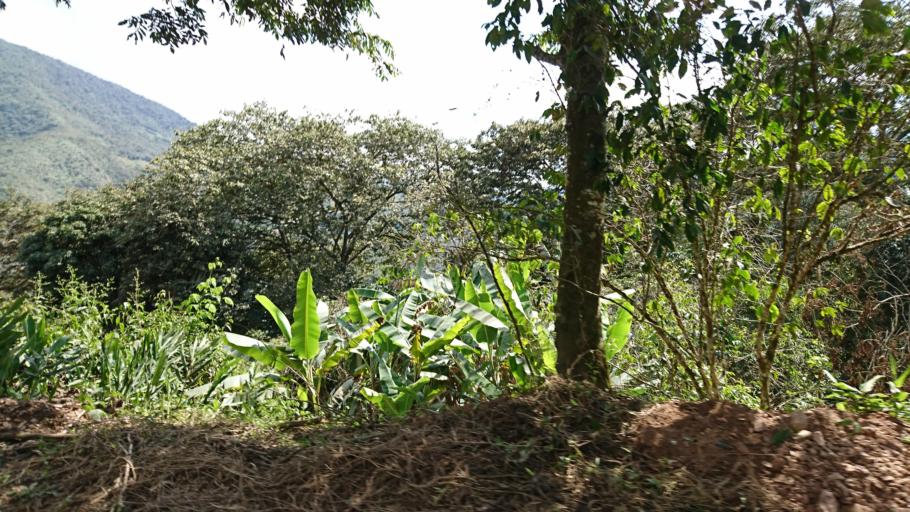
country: BO
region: La Paz
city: Coroico
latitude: -16.1276
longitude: -67.7559
